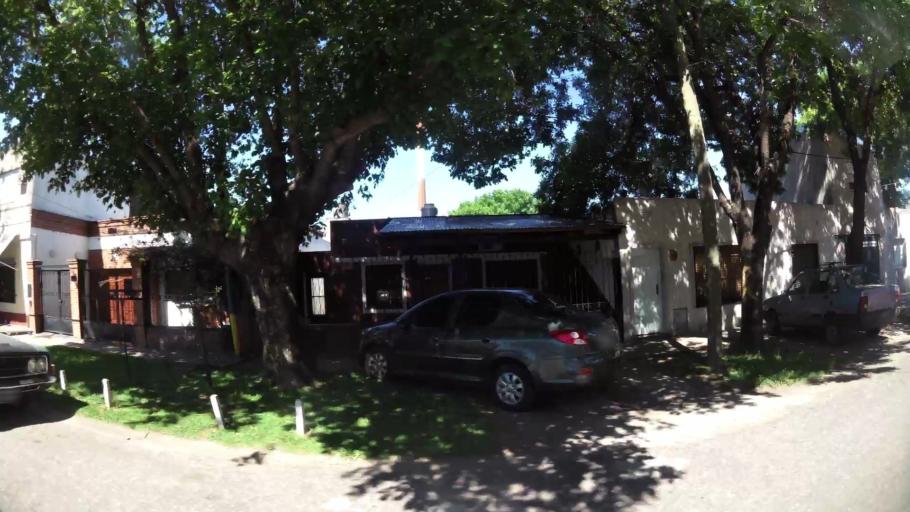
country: AR
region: Santa Fe
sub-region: Departamento de Rosario
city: Rosario
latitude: -32.9327
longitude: -60.6962
